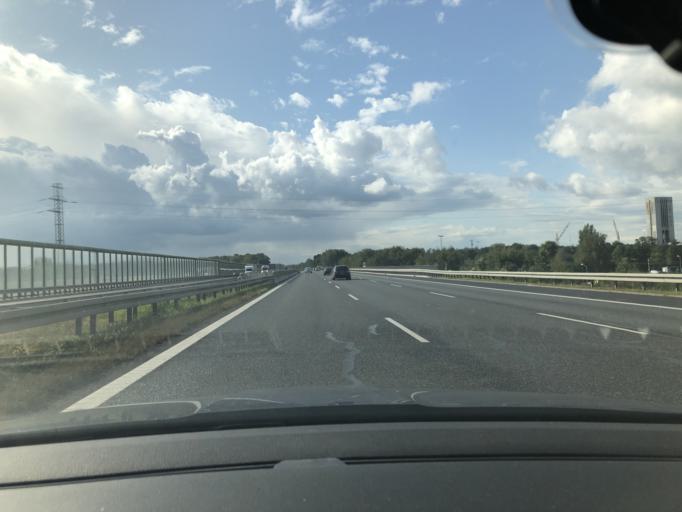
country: PL
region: Silesian Voivodeship
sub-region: Ruda Slaska
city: Ruda Slaska
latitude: 50.2579
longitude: 18.8418
